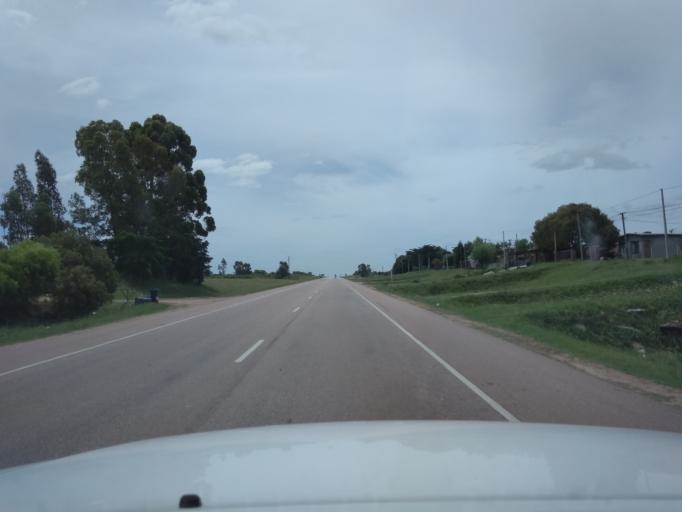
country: UY
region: Canelones
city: Canelones
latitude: -34.4948
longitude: -56.2819
